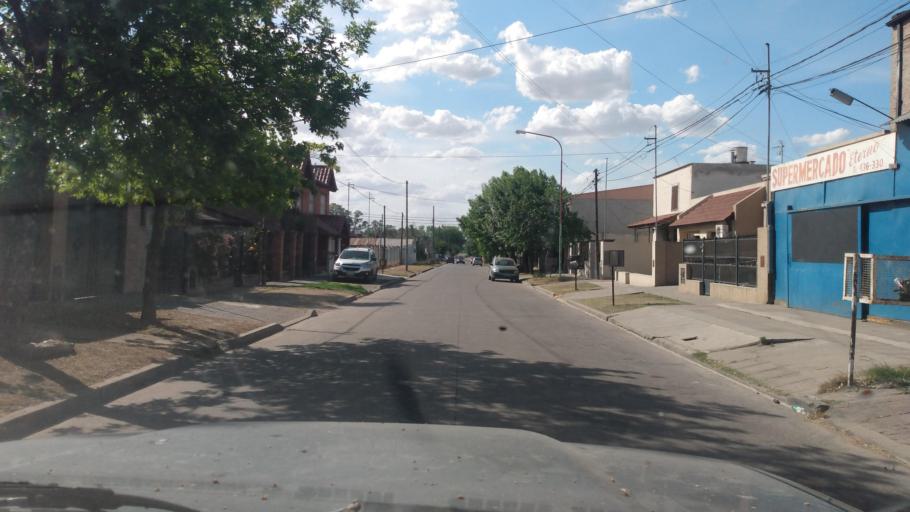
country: AR
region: Buenos Aires
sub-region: Partido de Lujan
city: Lujan
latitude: -34.5561
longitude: -59.1081
